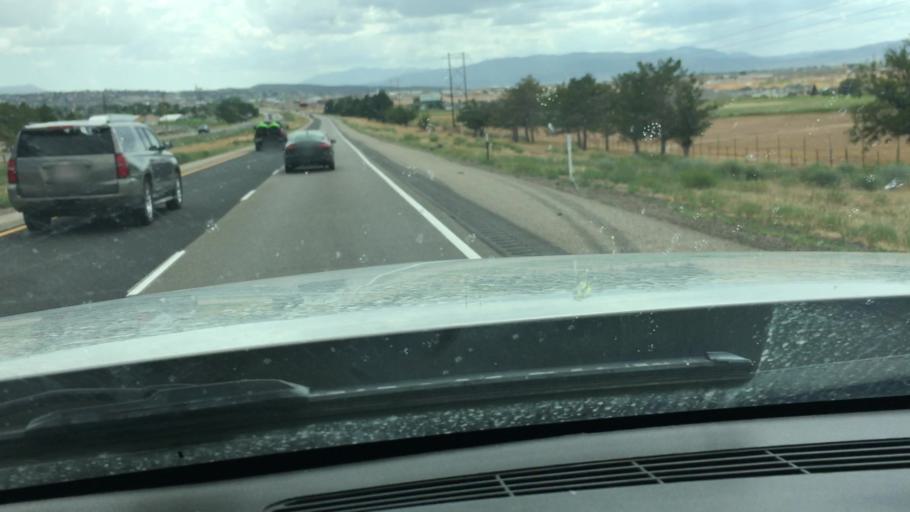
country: US
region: Utah
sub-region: Iron County
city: Cedar City
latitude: 37.7194
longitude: -113.0615
